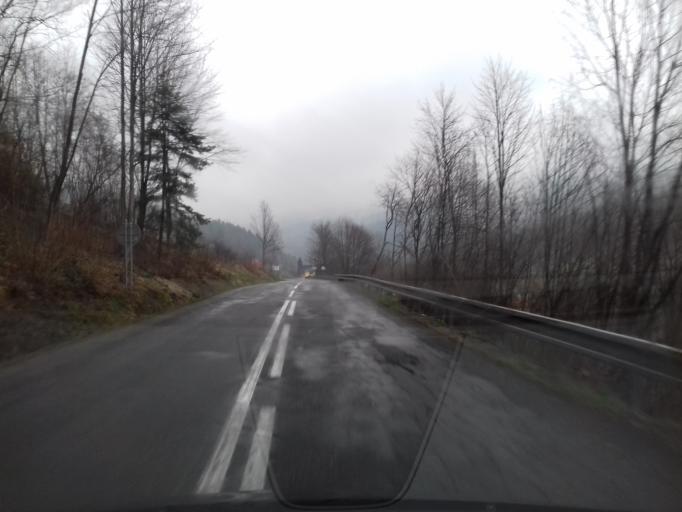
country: PL
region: Lesser Poland Voivodeship
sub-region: Powiat nowosadecki
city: Piwniczna-Zdroj
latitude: 49.3708
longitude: 20.6976
